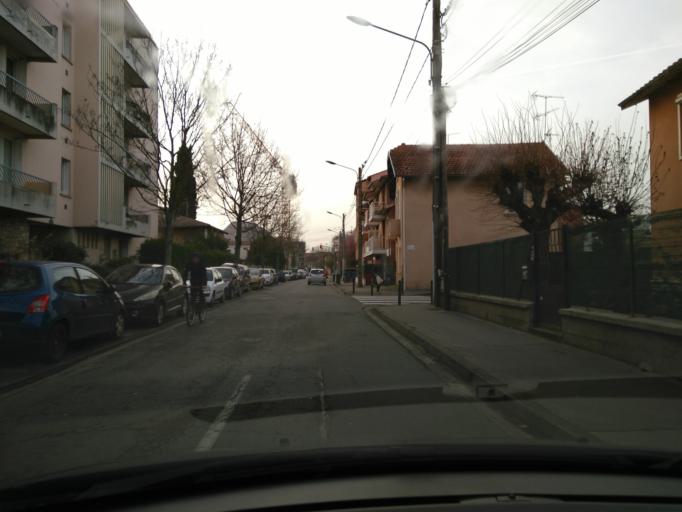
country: FR
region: Midi-Pyrenees
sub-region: Departement de la Haute-Garonne
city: Toulouse
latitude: 43.5770
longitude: 1.4535
